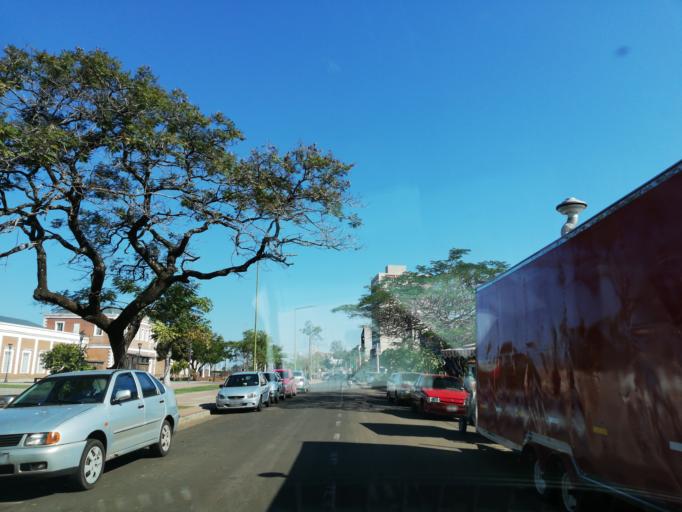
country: AR
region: Misiones
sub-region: Departamento de Capital
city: Posadas
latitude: -27.3696
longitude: -55.8857
